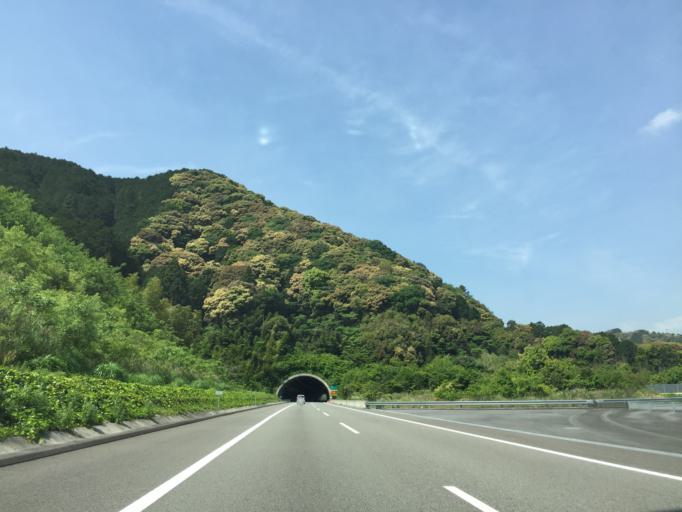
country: JP
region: Shizuoka
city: Fujieda
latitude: 34.8894
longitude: 138.2246
